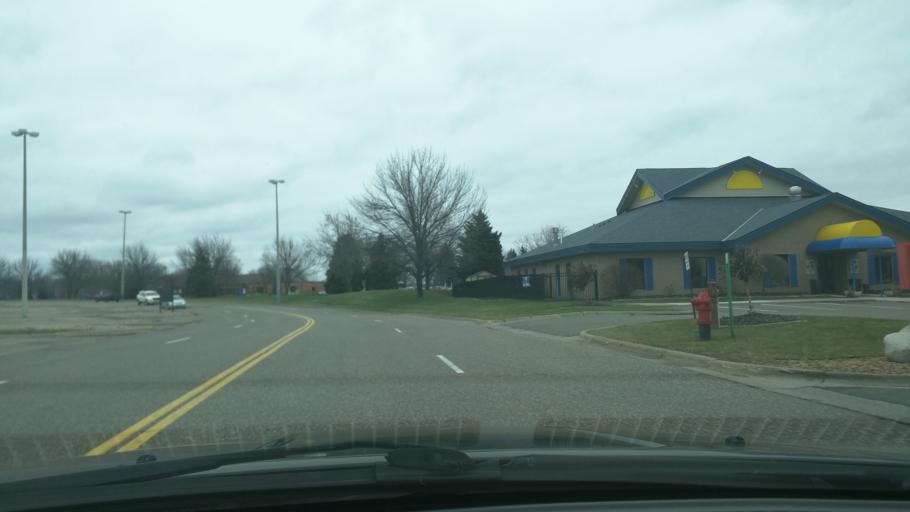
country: US
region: Minnesota
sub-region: Hennepin County
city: Eden Prairie
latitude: 44.8519
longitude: -93.4275
